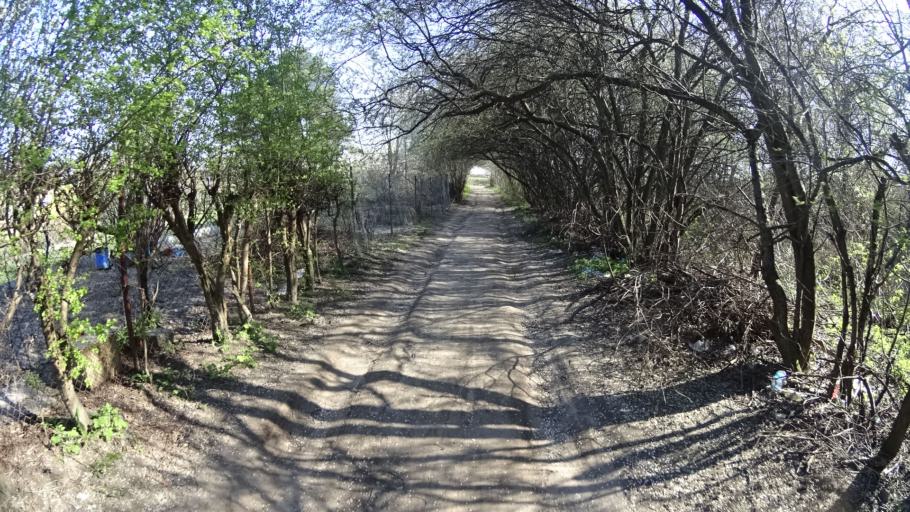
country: PL
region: Masovian Voivodeship
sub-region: Warszawa
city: Bemowo
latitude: 52.2458
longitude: 20.8913
